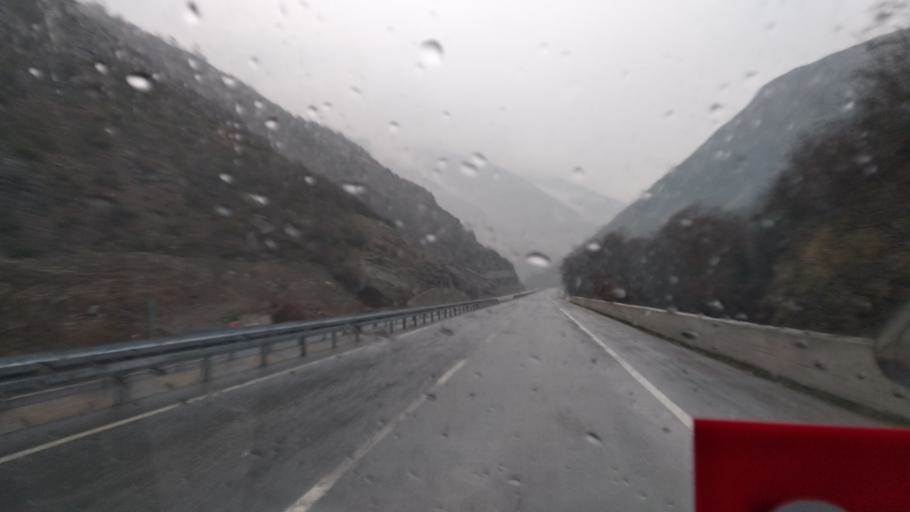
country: TR
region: Trabzon
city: Macka
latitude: 40.7905
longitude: 39.5805
